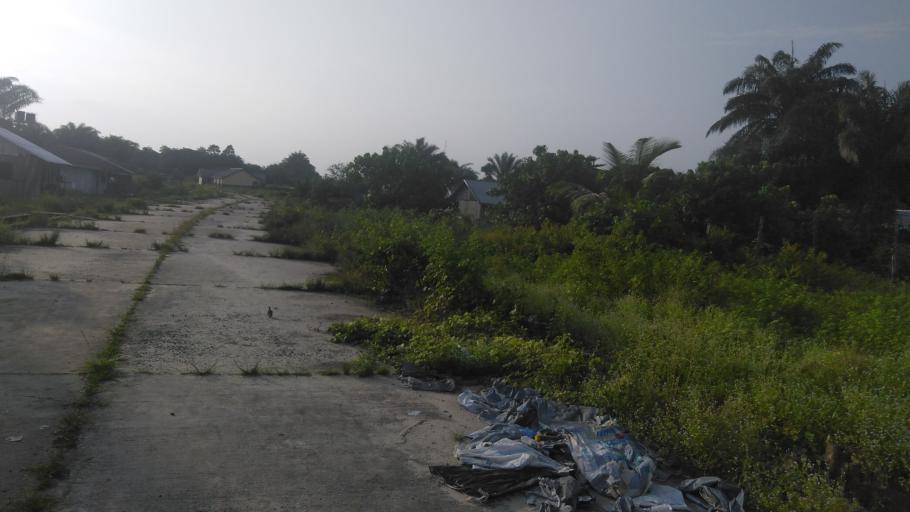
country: NG
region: Delta
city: Sapele
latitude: 5.8401
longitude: 5.1220
